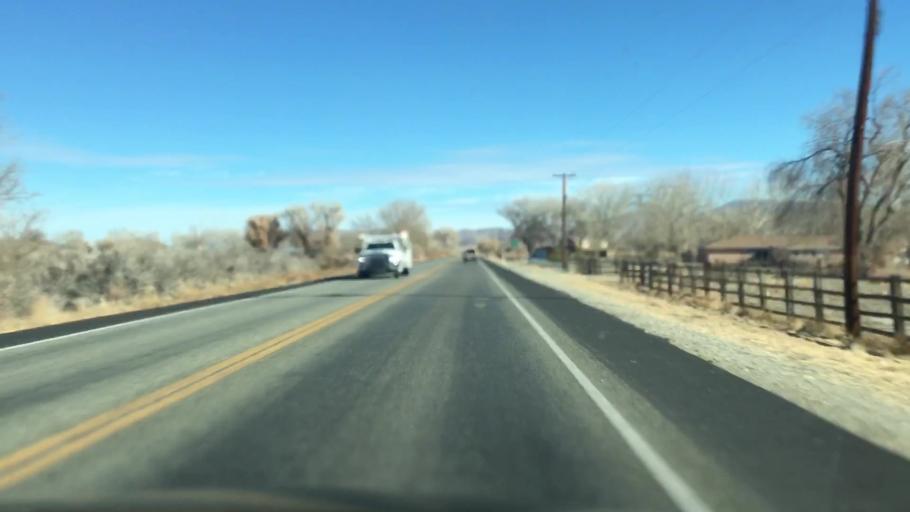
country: US
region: Nevada
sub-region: Lyon County
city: Yerington
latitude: 38.9975
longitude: -119.1484
